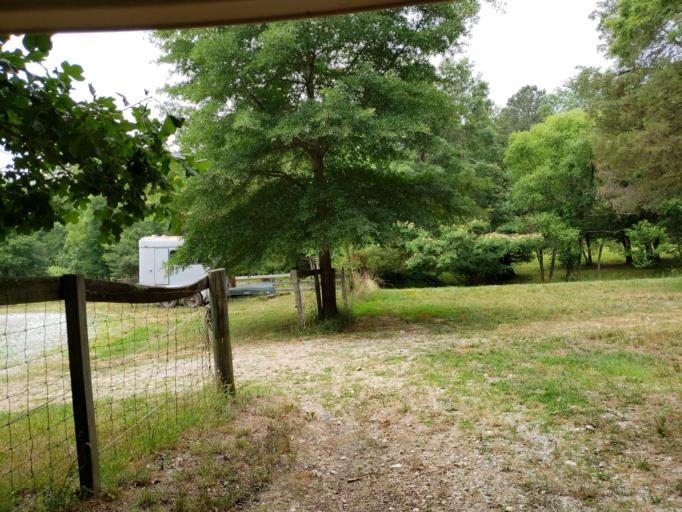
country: US
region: North Carolina
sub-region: Granville County
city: Butner
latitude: 36.1941
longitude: -78.8238
